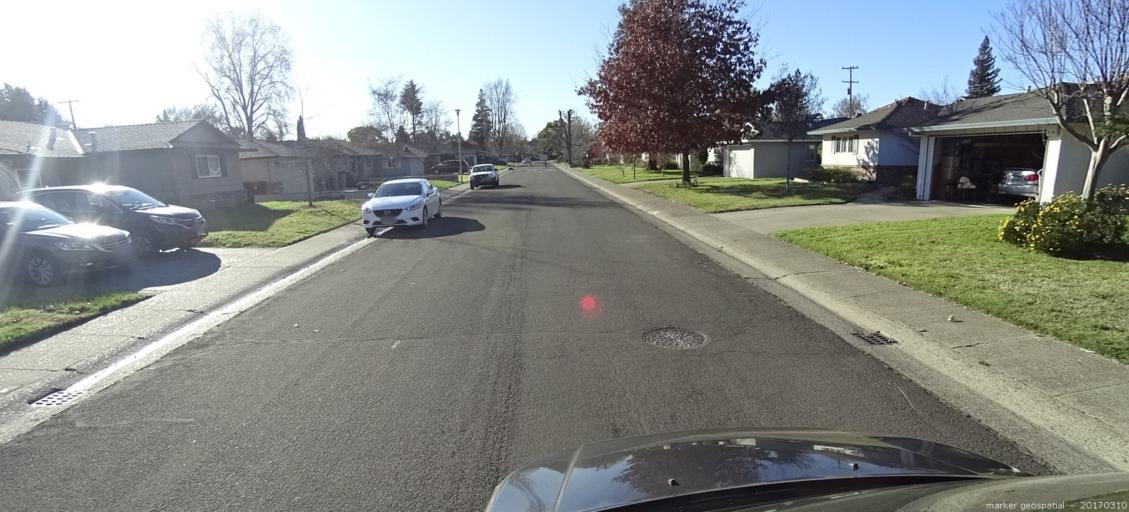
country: US
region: California
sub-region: Yolo County
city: West Sacramento
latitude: 38.5225
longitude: -121.5150
